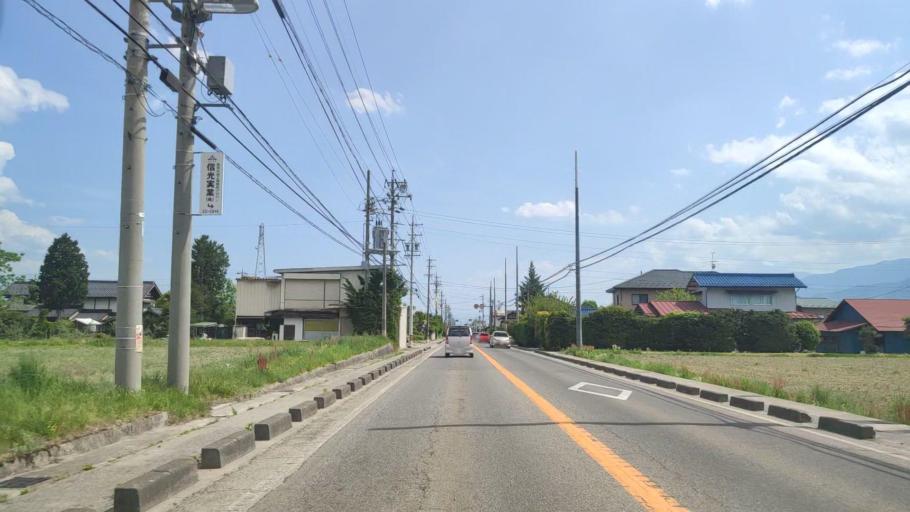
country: JP
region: Nagano
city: Omachi
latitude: 36.4617
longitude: 137.8502
